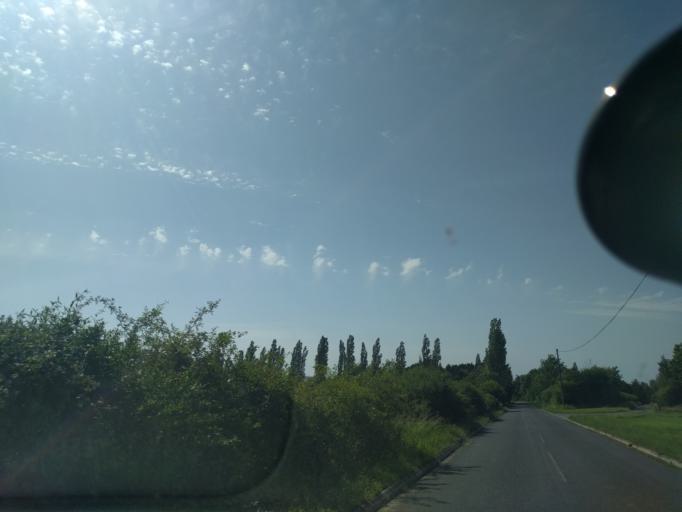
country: GB
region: England
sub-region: Wiltshire
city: Lyneham
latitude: 51.5327
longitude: -2.0003
